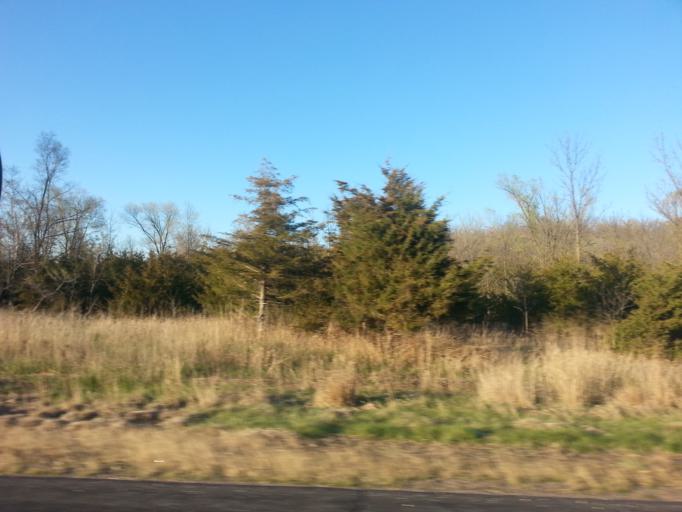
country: US
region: Minnesota
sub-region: Dakota County
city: Hastings
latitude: 44.6974
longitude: -92.8226
